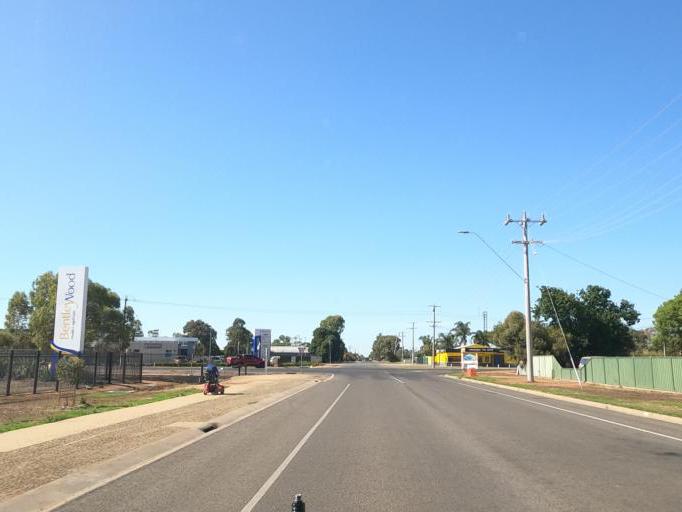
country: AU
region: Victoria
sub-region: Moira
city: Yarrawonga
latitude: -36.0143
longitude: 146.0132
